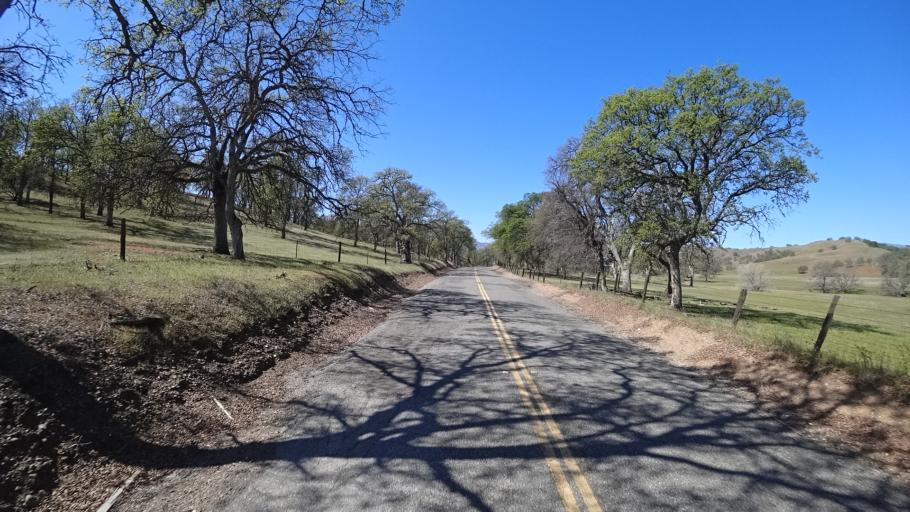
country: US
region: California
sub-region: Tehama County
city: Rancho Tehama Reserve
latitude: 39.7907
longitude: -122.4532
